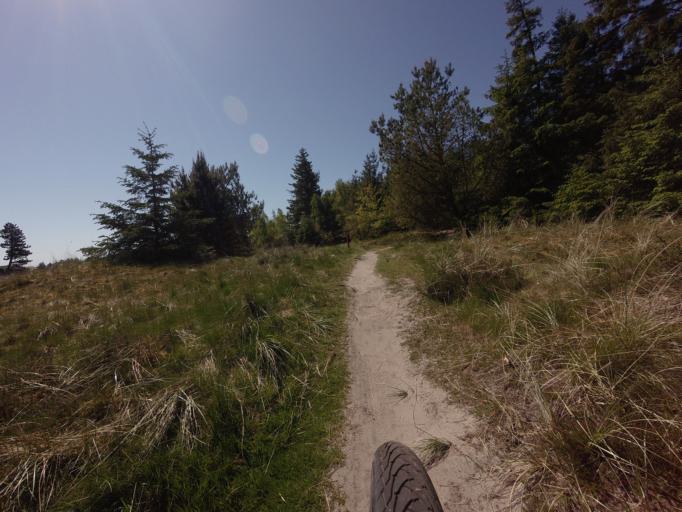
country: DK
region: North Denmark
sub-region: Jammerbugt Kommune
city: Pandrup
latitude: 57.2513
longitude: 9.6163
